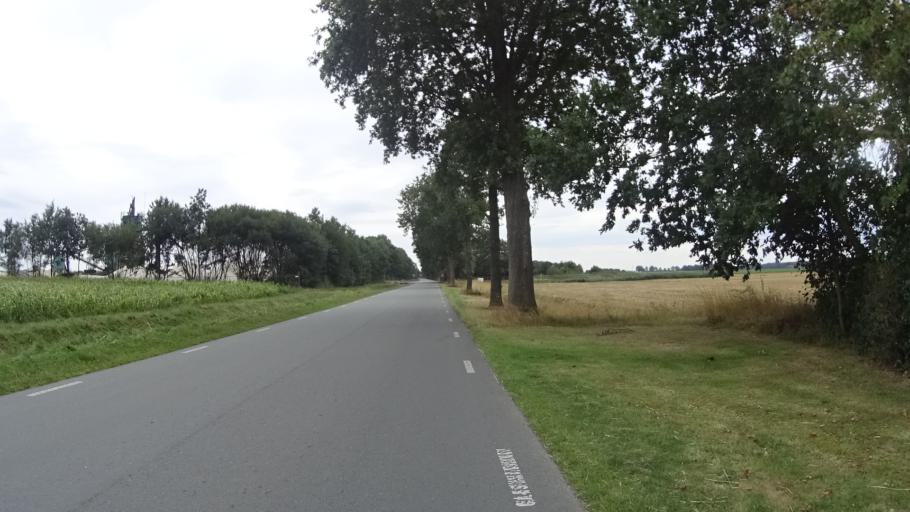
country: NL
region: Groningen
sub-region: Gemeente Slochteren
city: Slochteren
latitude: 53.1868
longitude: 6.8506
